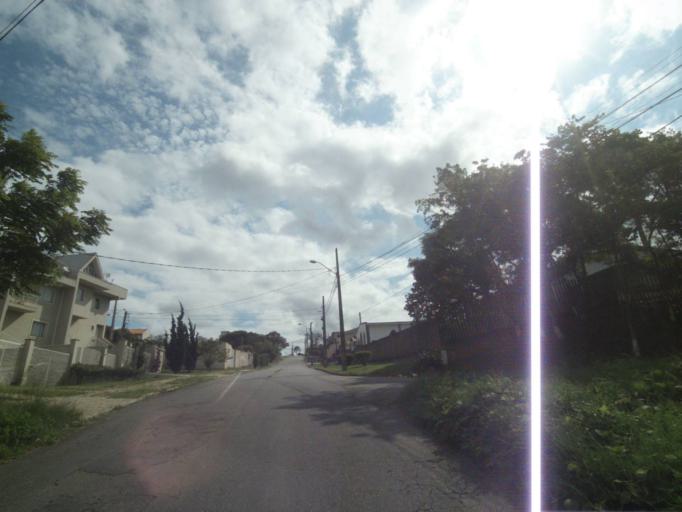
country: BR
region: Parana
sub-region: Curitiba
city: Curitiba
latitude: -25.3802
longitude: -49.2943
